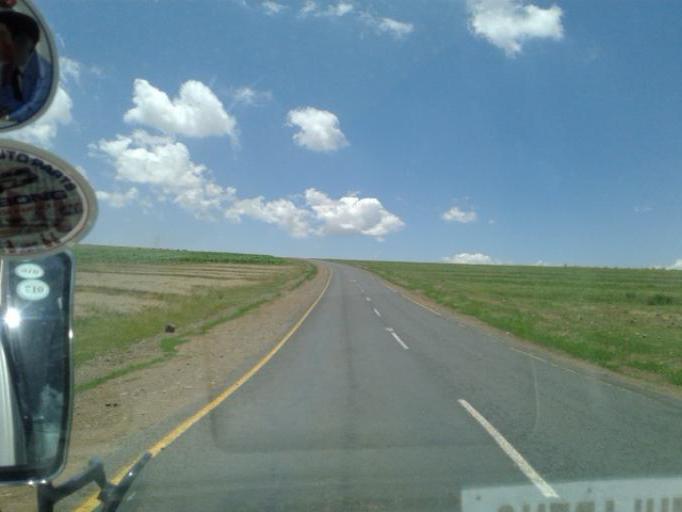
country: LS
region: Maseru
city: Maseru
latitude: -29.3053
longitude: 27.6074
